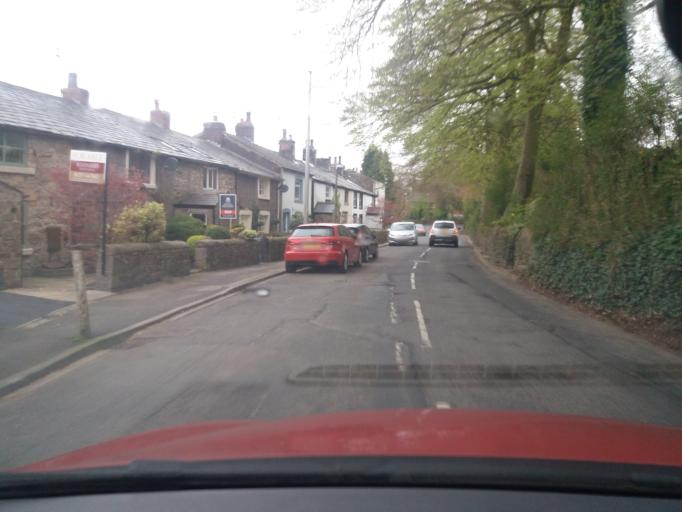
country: GB
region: England
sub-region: Lancashire
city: Clayton-le-Woods
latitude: 53.6852
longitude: -2.6364
